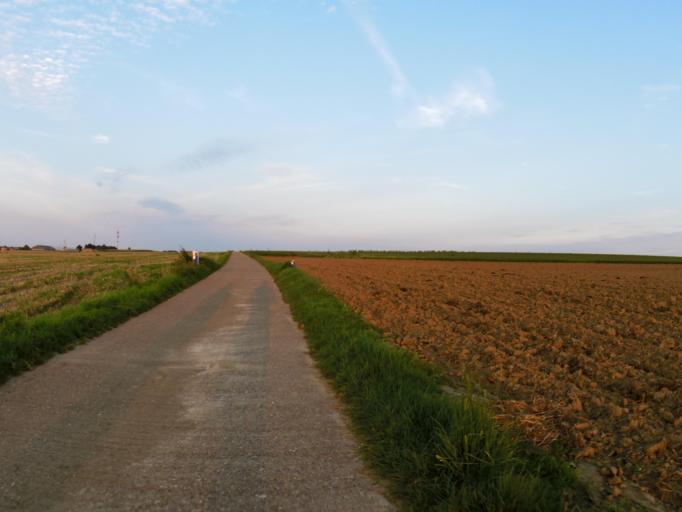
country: BE
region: Wallonia
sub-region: Province de Liege
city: Juprelle
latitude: 50.7649
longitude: 5.5451
